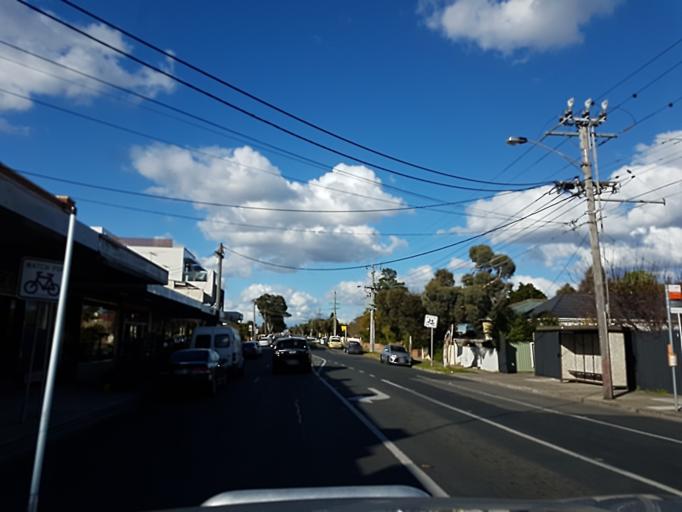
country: AU
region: Victoria
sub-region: Darebin
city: Thornbury
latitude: -37.7646
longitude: 145.0124
